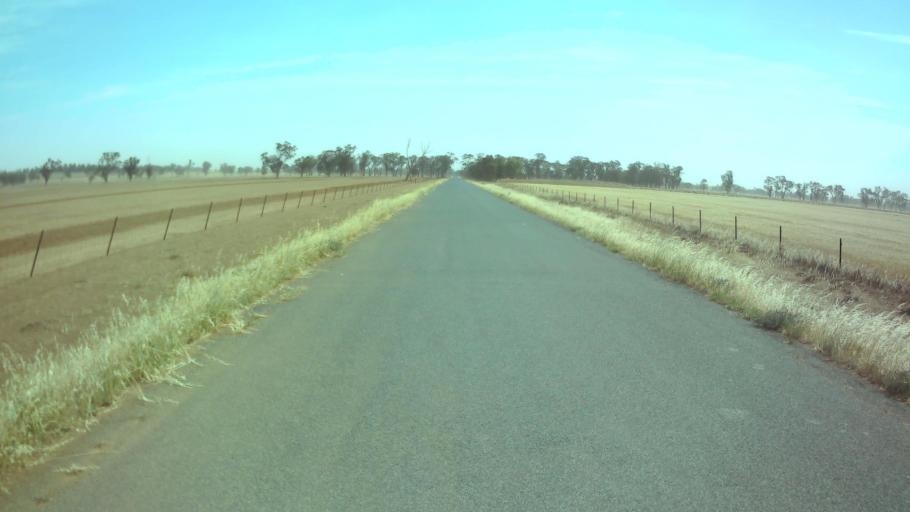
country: AU
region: New South Wales
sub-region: Weddin
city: Grenfell
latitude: -33.7217
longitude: 147.9997
